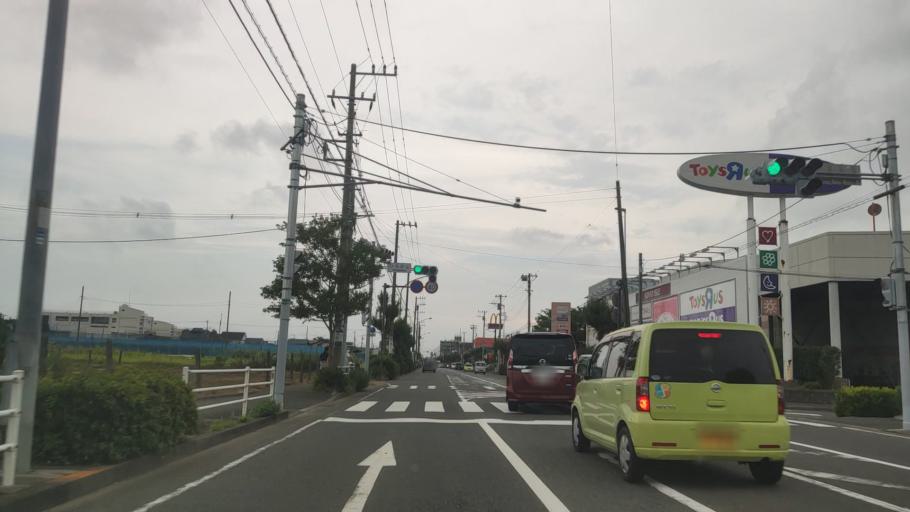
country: JP
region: Kanagawa
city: Minami-rinkan
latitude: 35.4484
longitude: 139.4840
